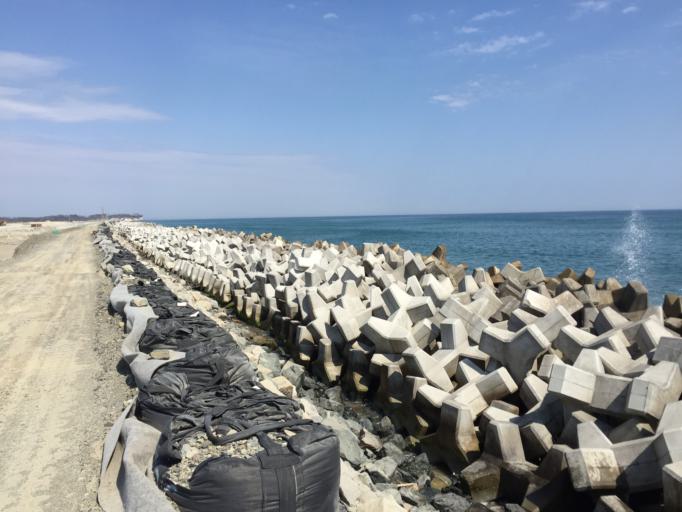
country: JP
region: Miyagi
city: Marumori
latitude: 37.7943
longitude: 140.9864
